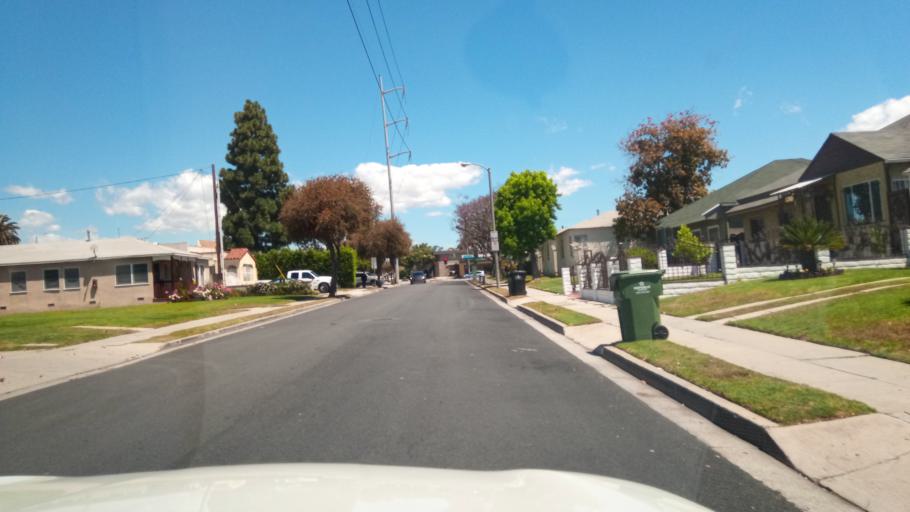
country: US
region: California
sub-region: Los Angeles County
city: Inglewood
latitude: 33.9753
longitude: -118.3595
